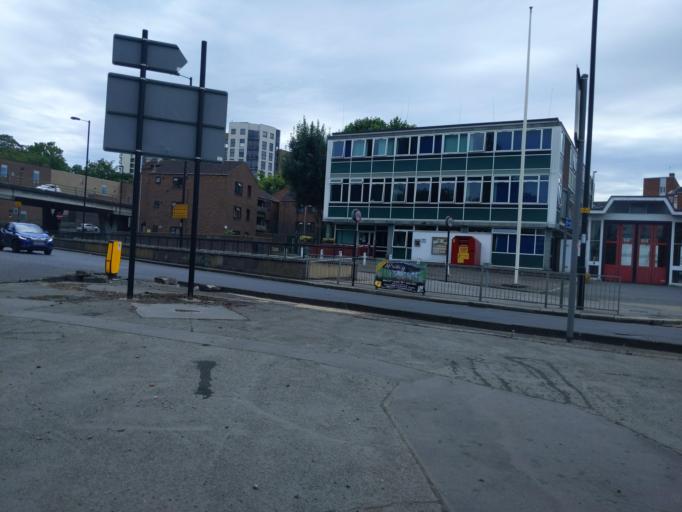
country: GB
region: England
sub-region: Greater London
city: South Croydon
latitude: 51.3690
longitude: -0.1045
